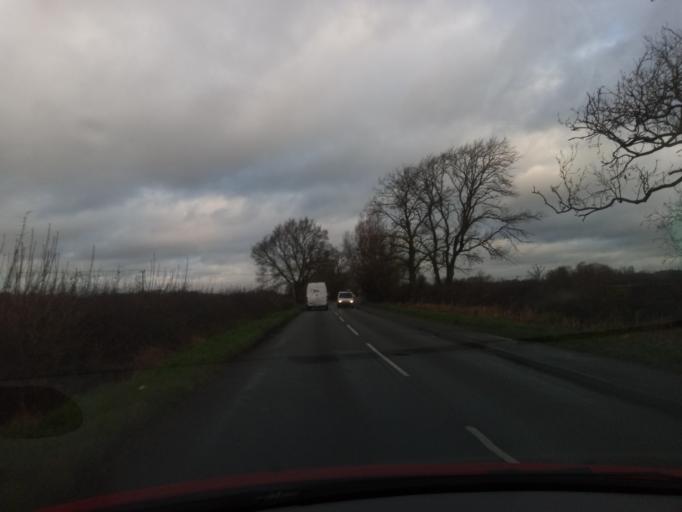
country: GB
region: England
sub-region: Leicestershire
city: Sileby
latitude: 52.7316
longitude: -1.1270
